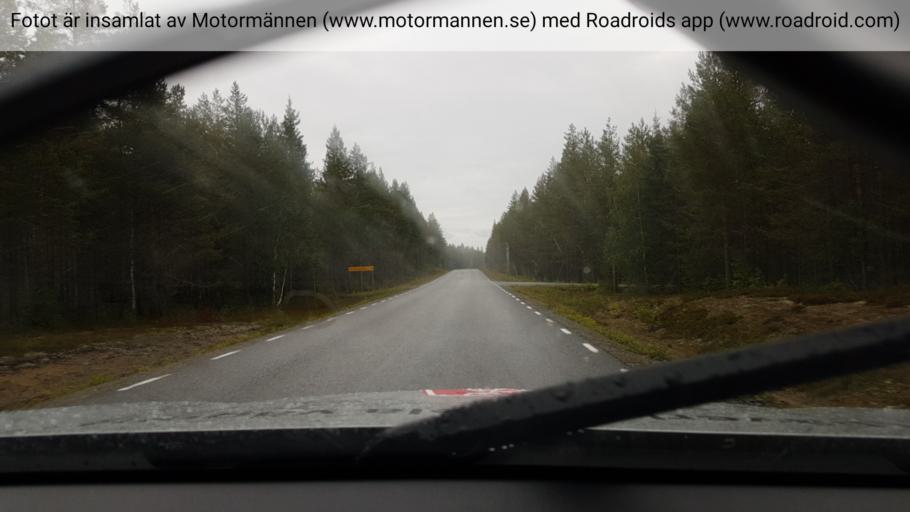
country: SE
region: Vaesterbotten
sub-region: Skelleftea Kommun
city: Langsele
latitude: 64.5472
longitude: 20.2160
